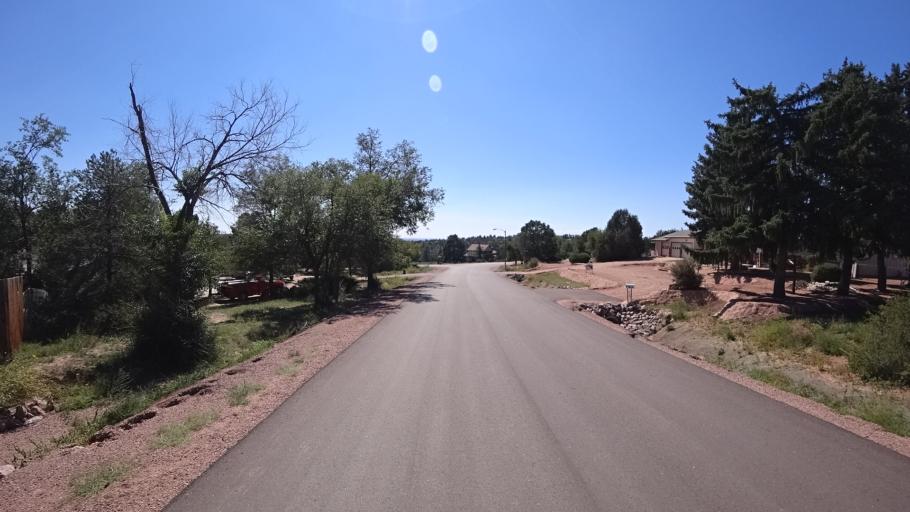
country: US
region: Colorado
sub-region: El Paso County
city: Cimarron Hills
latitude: 38.8669
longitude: -104.7376
